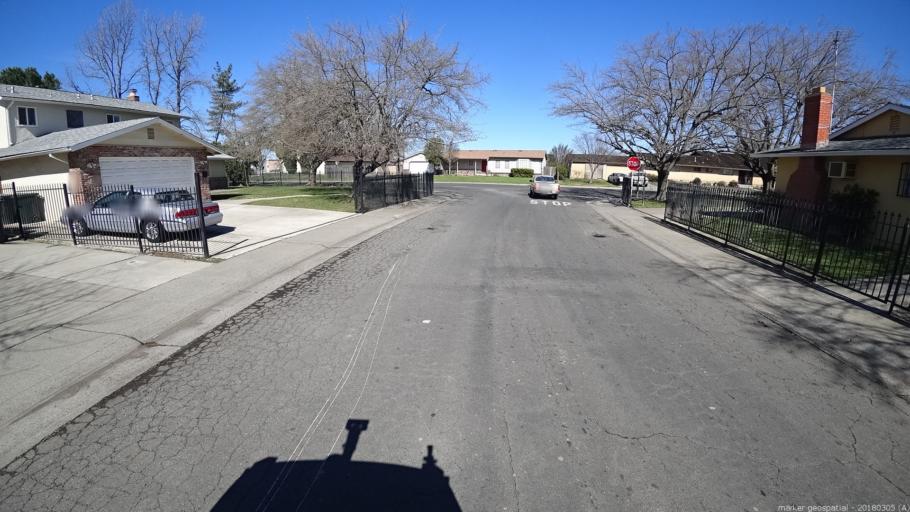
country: US
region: California
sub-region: Sacramento County
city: Florin
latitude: 38.5019
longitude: -121.4267
